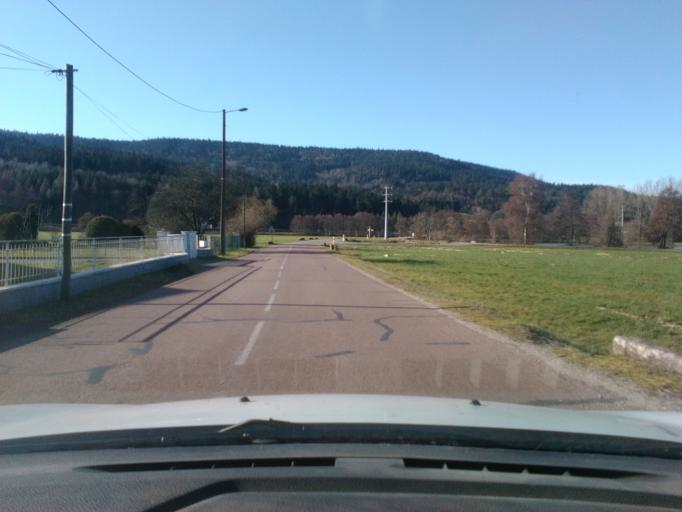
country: FR
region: Lorraine
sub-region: Departement des Vosges
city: Vecoux
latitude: 47.9843
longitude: 6.6270
